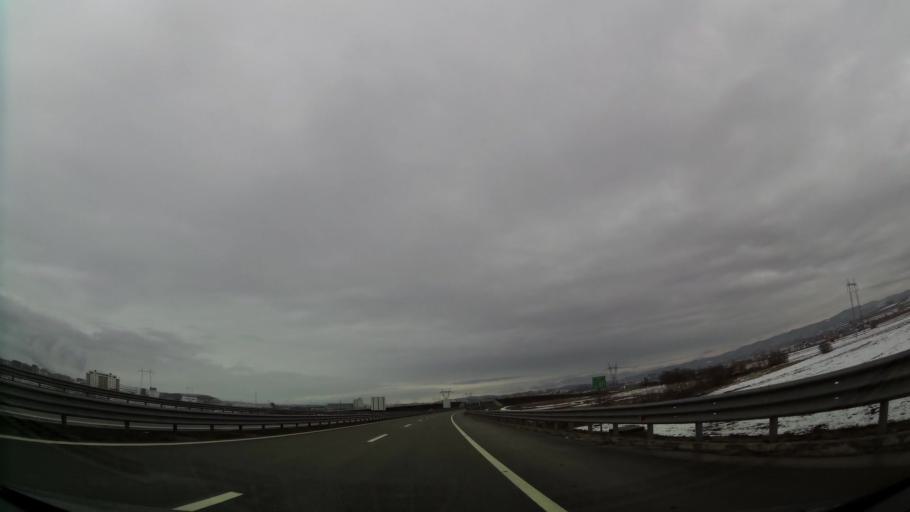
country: XK
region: Pristina
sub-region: Kosovo Polje
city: Kosovo Polje
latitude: 42.6296
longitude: 21.1178
